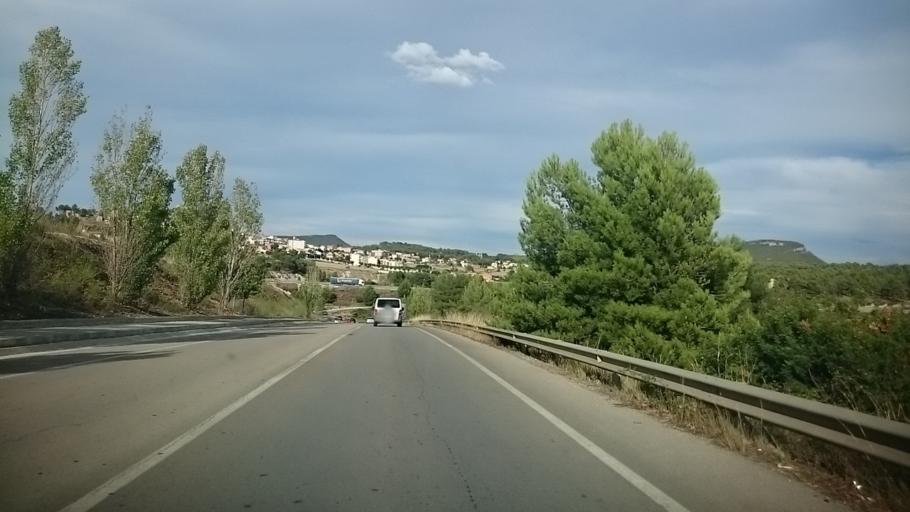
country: ES
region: Catalonia
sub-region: Provincia de Barcelona
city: Odena
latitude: 41.5971
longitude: 1.6332
